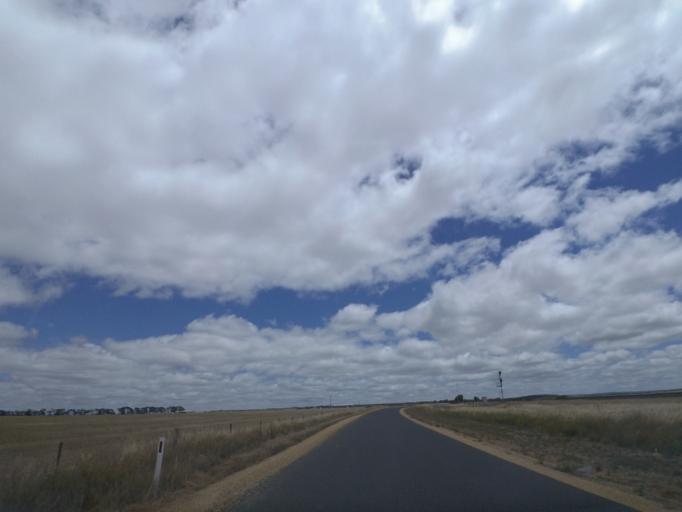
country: AU
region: Victoria
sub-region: Moorabool
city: Bacchus Marsh
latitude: -37.6833
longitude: 144.3569
